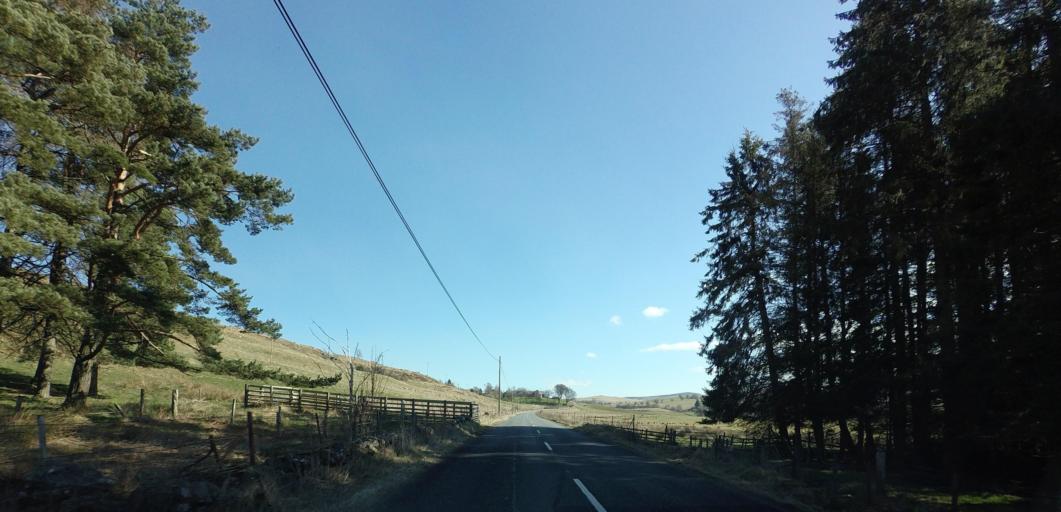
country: GB
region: Scotland
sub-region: Perth and Kinross
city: Aberfeldy
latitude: 56.5274
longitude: -3.7394
